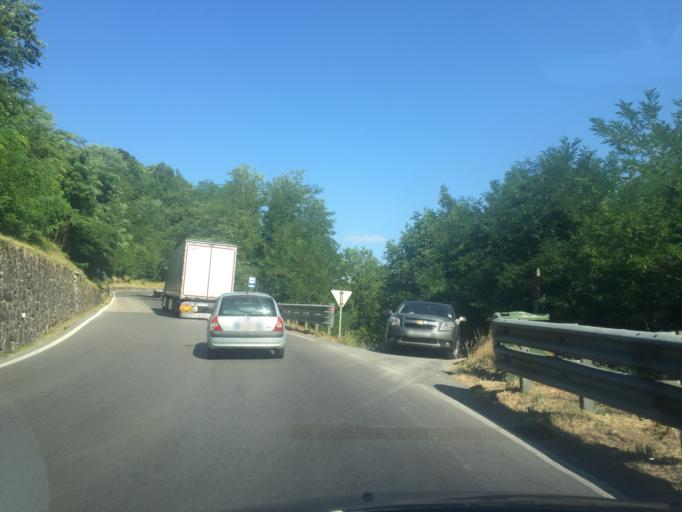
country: IT
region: Tuscany
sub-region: Provincia di Lucca
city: San Romano in Garfagnana
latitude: 44.1435
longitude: 10.3601
